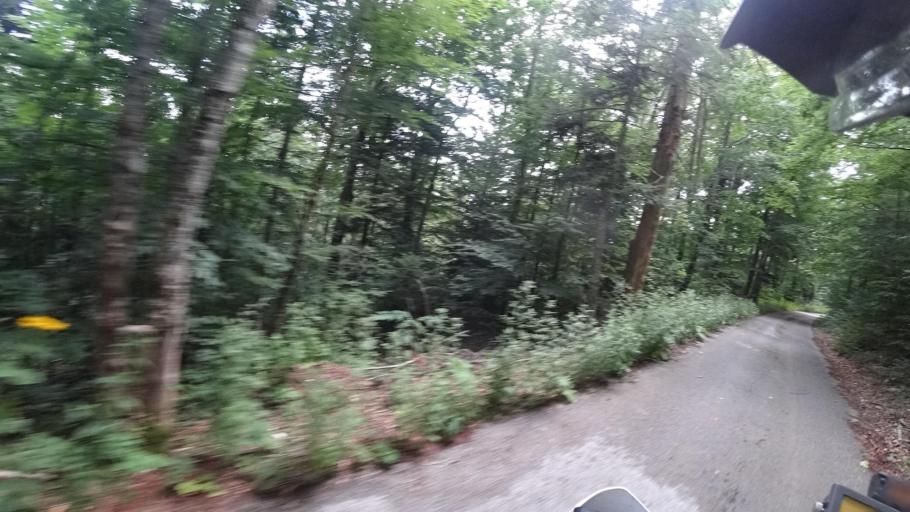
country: HR
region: Licko-Senjska
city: Senj
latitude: 45.1147
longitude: 14.9450
